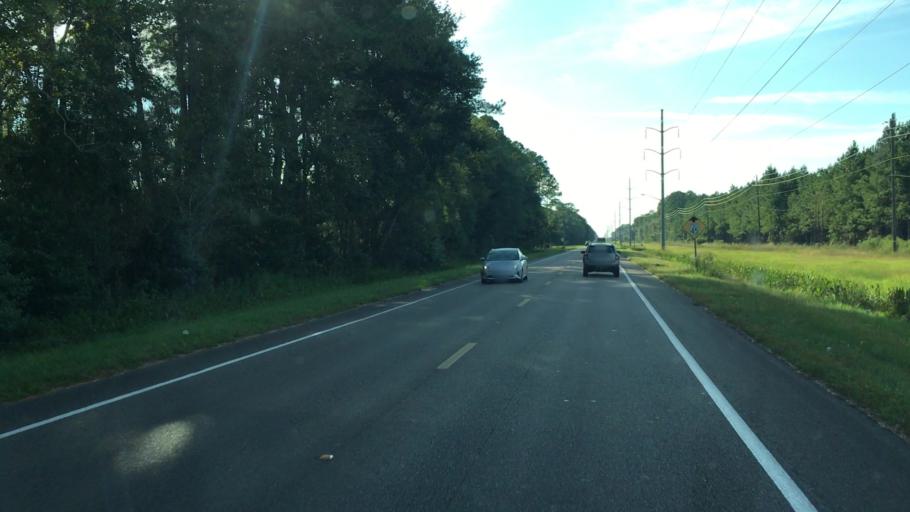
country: US
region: Florida
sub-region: Alachua County
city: Gainesville
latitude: 29.7032
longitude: -82.3271
